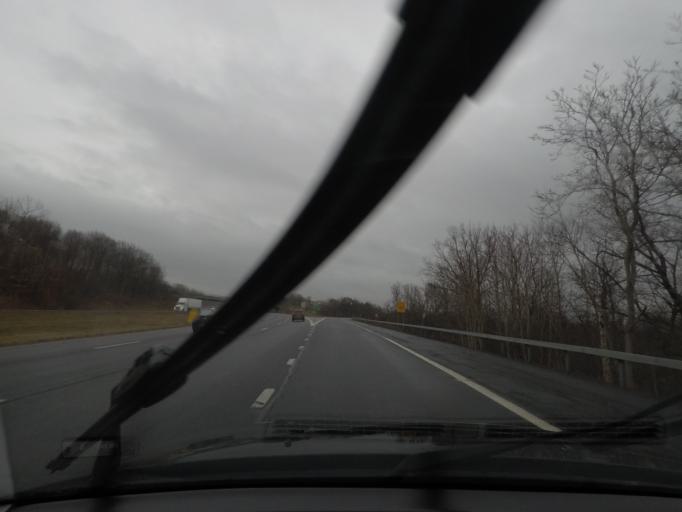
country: US
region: New York
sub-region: Rensselaer County
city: Hampton Manor
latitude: 42.6291
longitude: -73.7034
